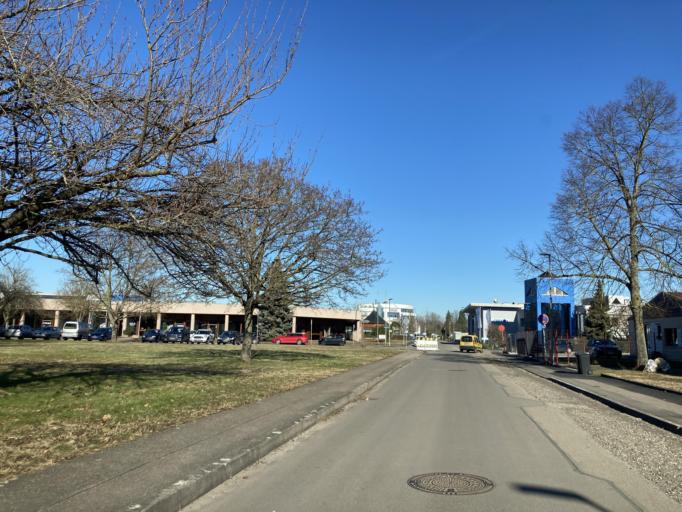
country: DE
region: Baden-Wuerttemberg
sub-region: Freiburg Region
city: Bahlingen
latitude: 48.1215
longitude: 7.7482
